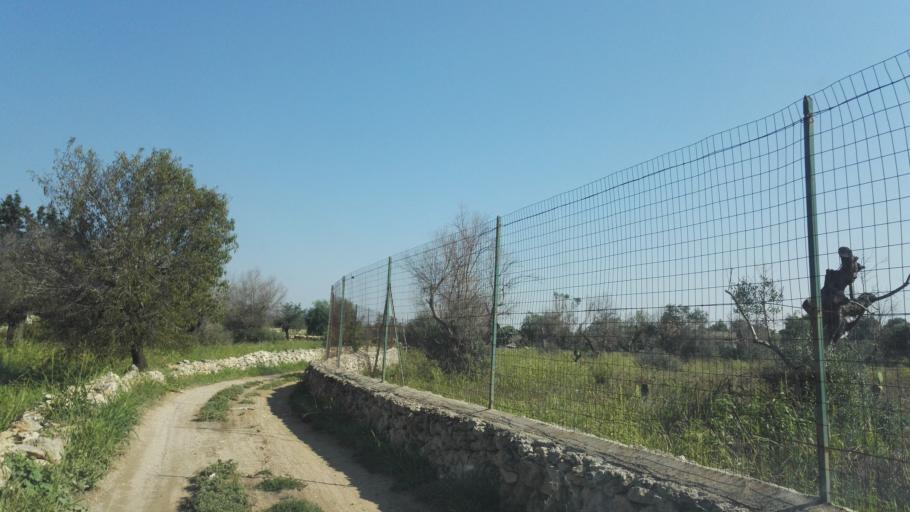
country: IT
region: Apulia
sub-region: Provincia di Lecce
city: Alezio
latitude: 40.0526
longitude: 18.0394
